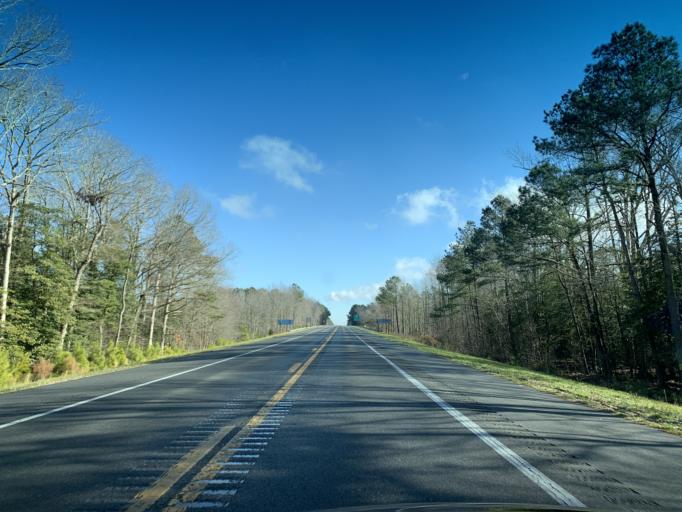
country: US
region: Maryland
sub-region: Worcester County
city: Berlin
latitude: 38.3771
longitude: -75.2180
